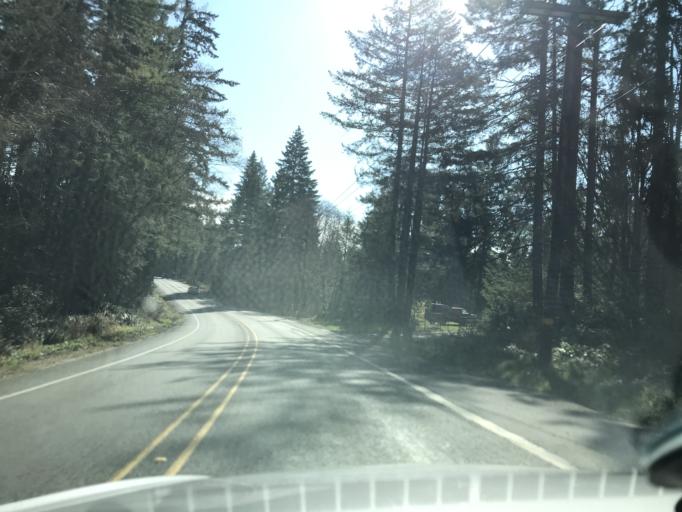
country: US
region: Washington
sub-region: Pierce County
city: Key Center
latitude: 47.3305
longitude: -122.7533
